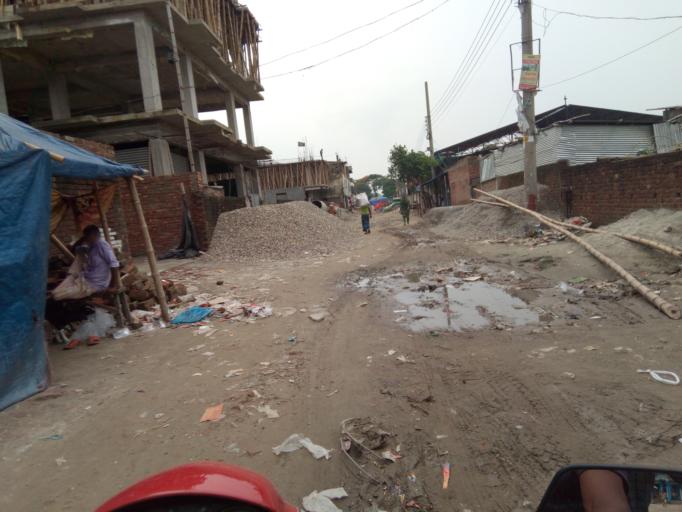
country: BD
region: Dhaka
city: Azimpur
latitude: 23.7592
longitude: 90.3516
